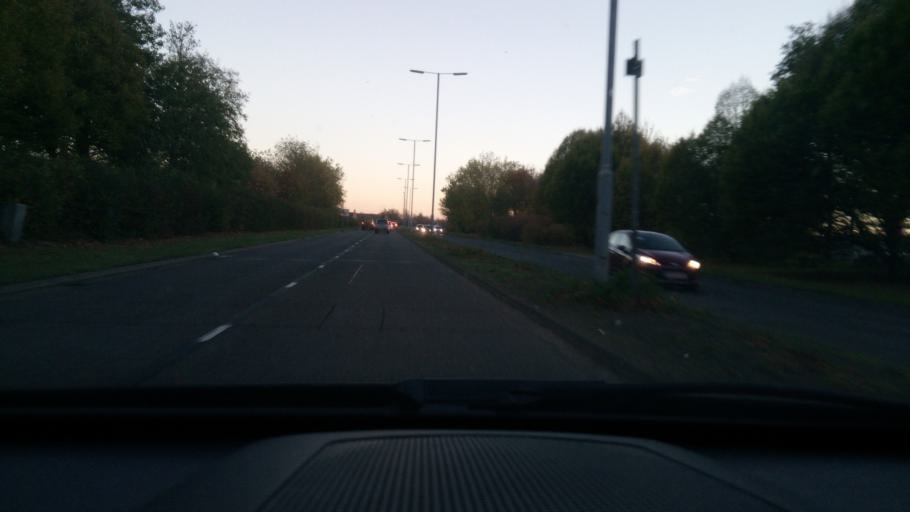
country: GB
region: England
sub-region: Peterborough
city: Peterborough
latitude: 52.5858
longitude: -0.2547
